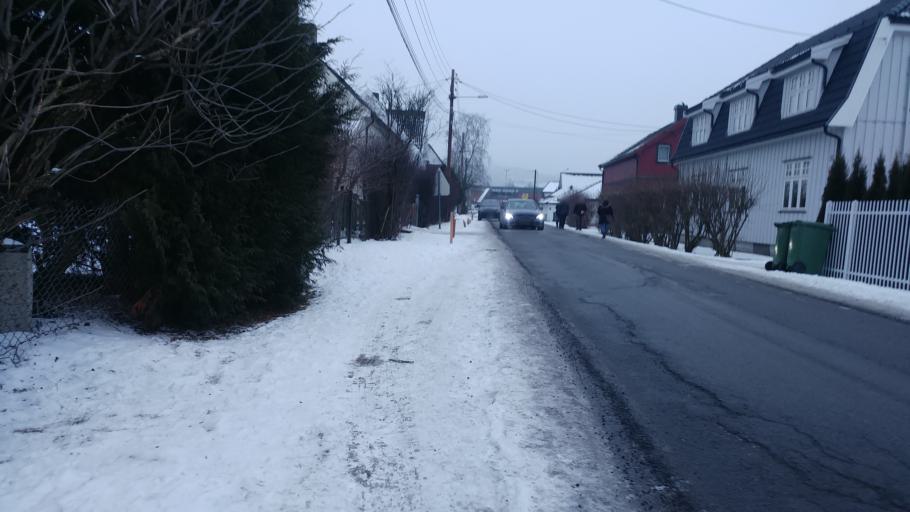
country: NO
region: Akershus
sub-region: Skedsmo
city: Lillestrom
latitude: 59.9592
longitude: 11.0379
